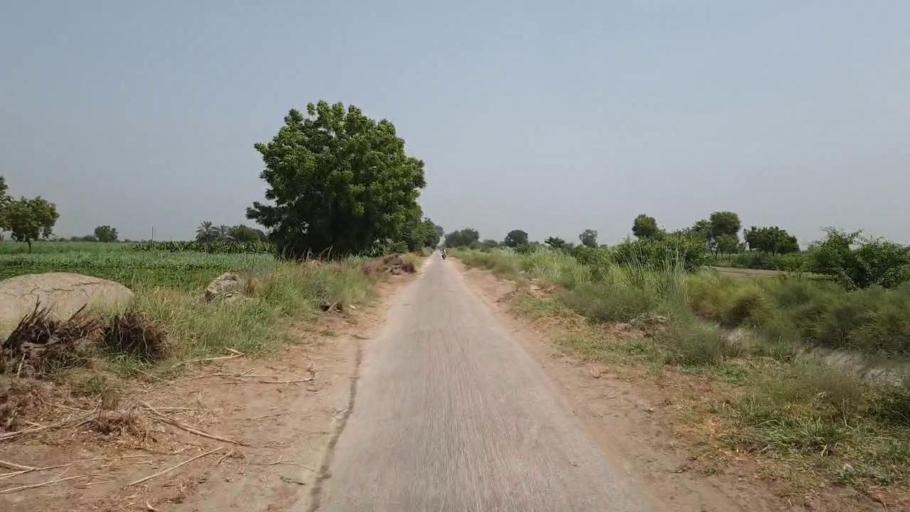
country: PK
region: Sindh
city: Nawabshah
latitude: 26.2791
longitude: 68.3126
